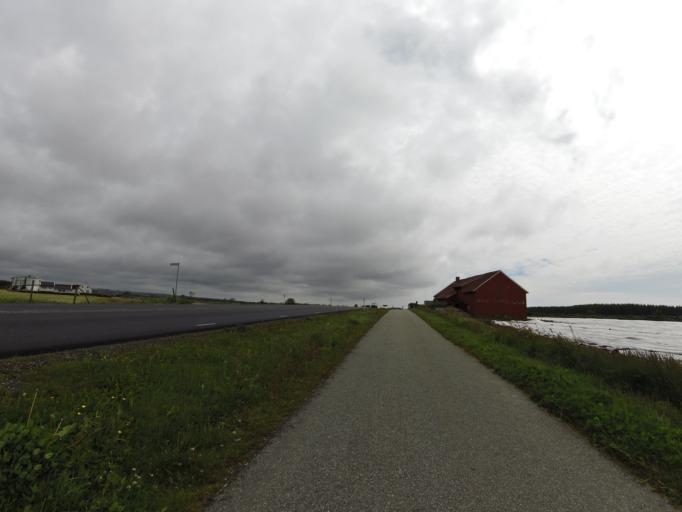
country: NO
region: Rogaland
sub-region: Ha
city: Naerbo
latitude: 58.6399
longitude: 5.6070
